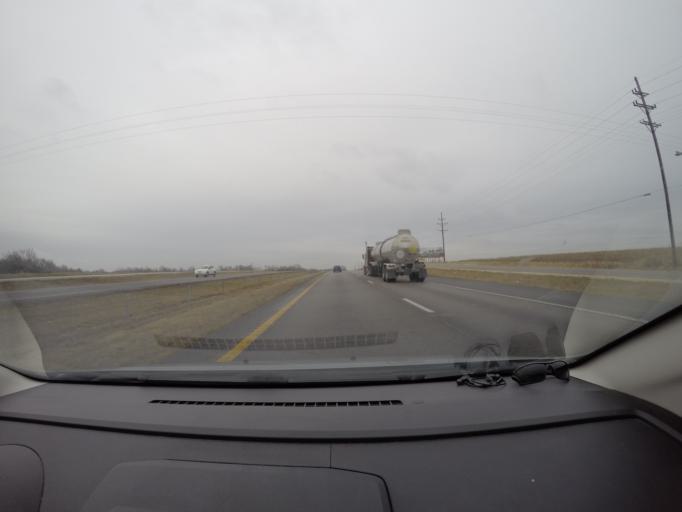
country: US
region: Missouri
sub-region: Warren County
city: Warrenton
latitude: 38.8460
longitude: -91.2556
